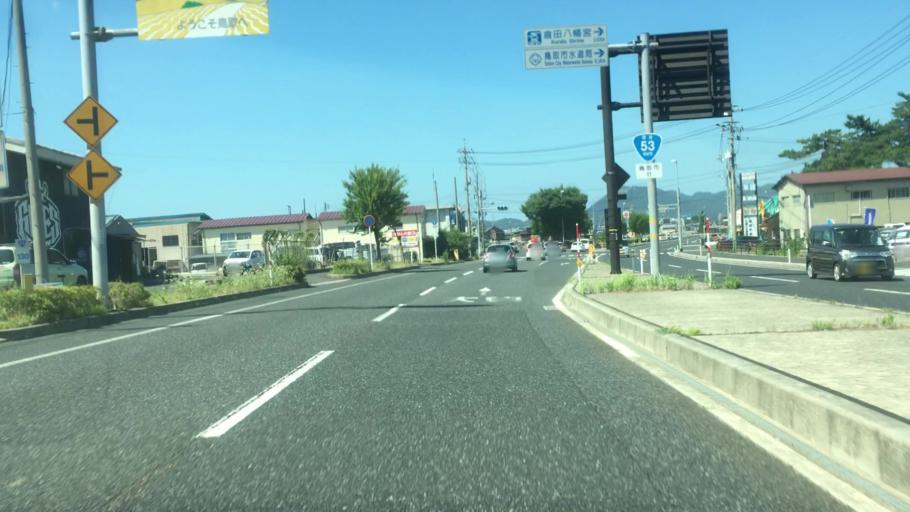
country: JP
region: Tottori
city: Tottori
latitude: 35.4667
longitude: 134.2148
